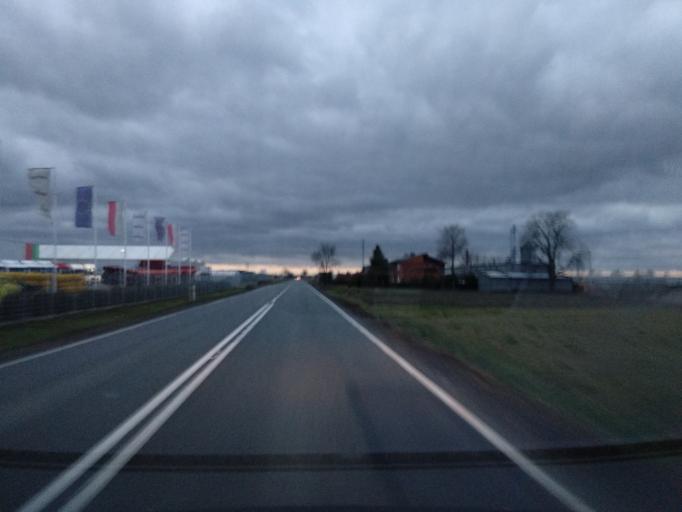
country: PL
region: Greater Poland Voivodeship
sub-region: Powiat kaliski
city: Stawiszyn
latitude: 51.8580
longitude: 18.0977
